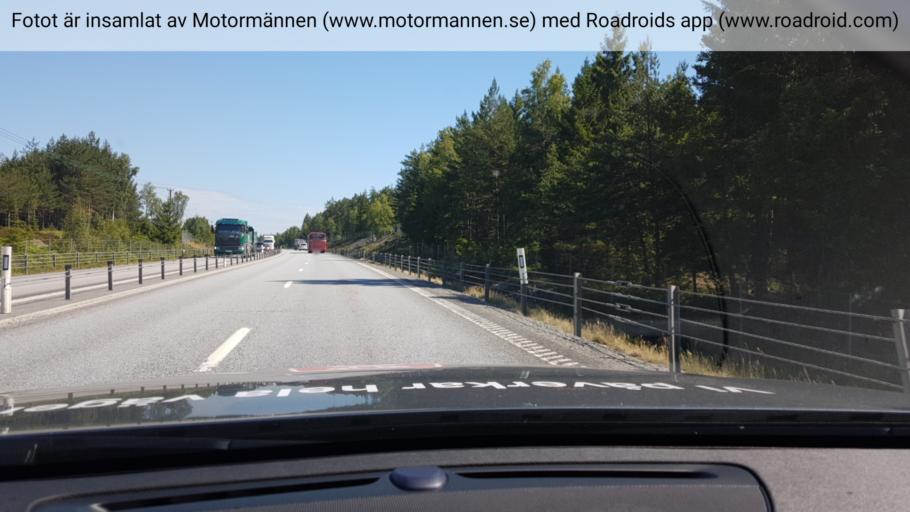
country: SE
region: Stockholm
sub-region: Osterakers Kommun
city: Akersberga
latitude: 59.5927
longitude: 18.2665
